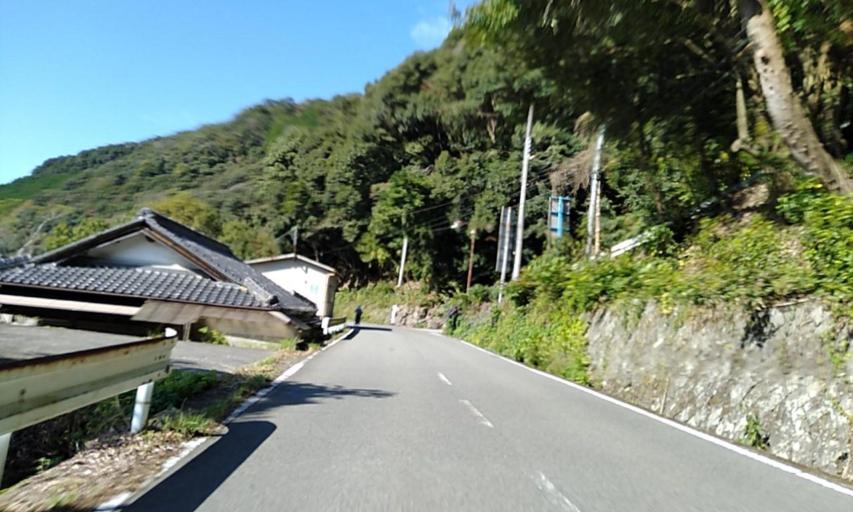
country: JP
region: Wakayama
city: Kainan
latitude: 34.0566
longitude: 135.3340
